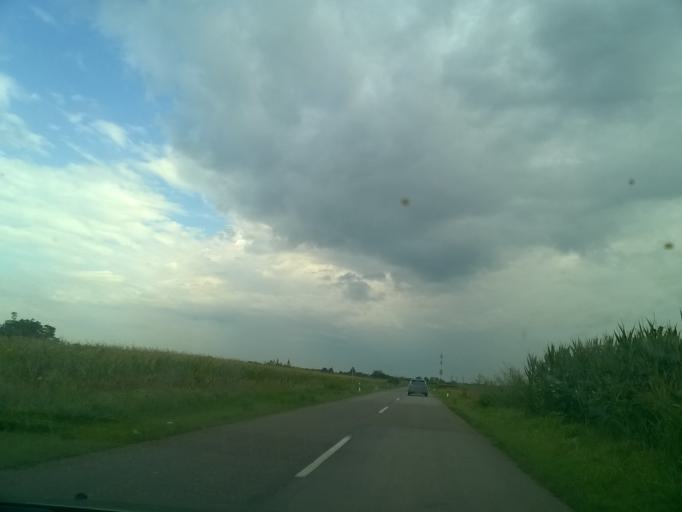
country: RS
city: Tomasevac
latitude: 45.2547
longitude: 20.6295
